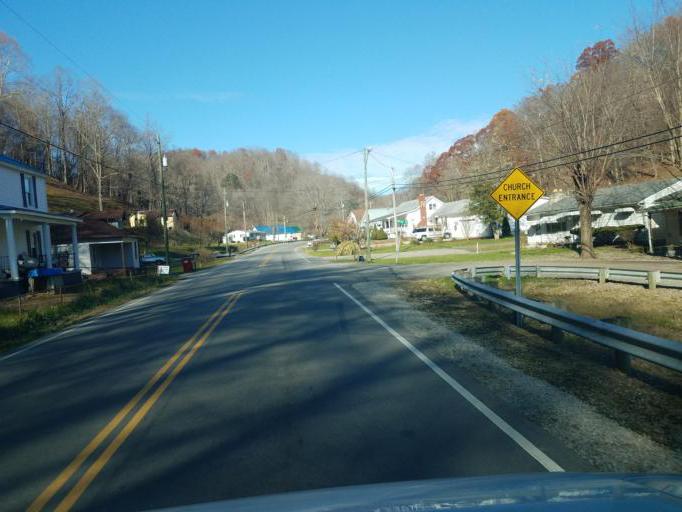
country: US
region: Ohio
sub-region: Scioto County
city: Rosemount
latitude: 38.7886
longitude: -82.9518
